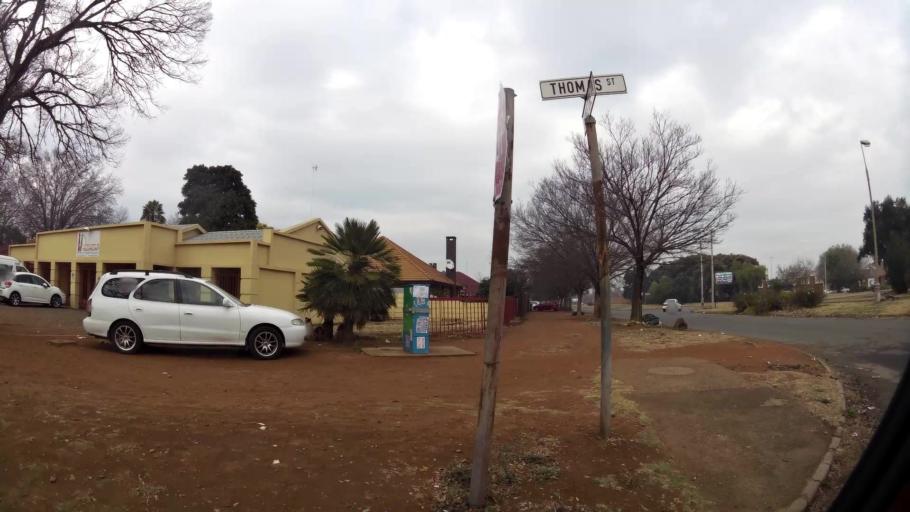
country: ZA
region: Gauteng
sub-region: Sedibeng District Municipality
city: Vanderbijlpark
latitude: -26.6997
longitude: 27.8406
